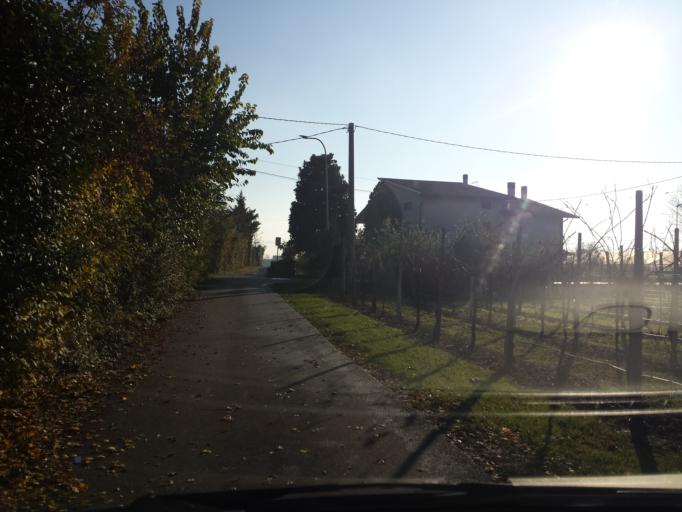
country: IT
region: Veneto
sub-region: Provincia di Vicenza
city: Sandrigo
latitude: 45.6820
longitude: 11.5842
